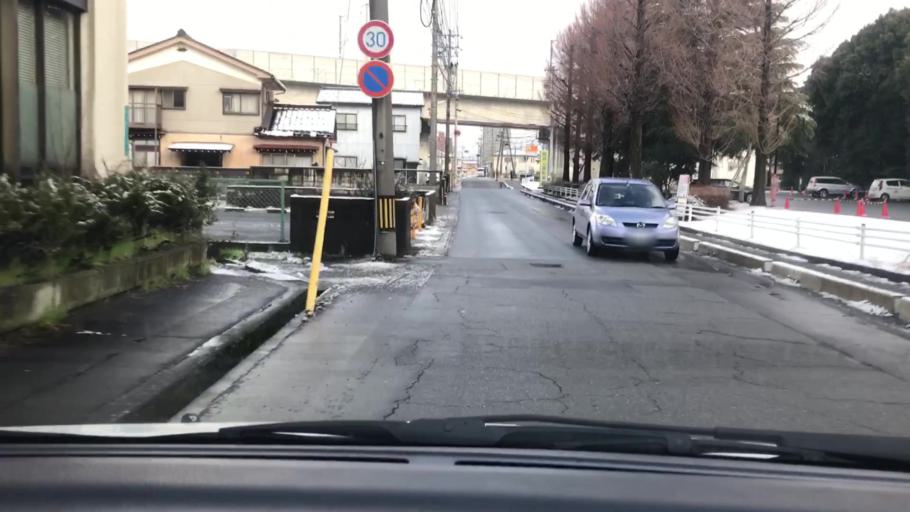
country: JP
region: Toyama
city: Toyama-shi
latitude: 36.6980
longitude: 137.2296
